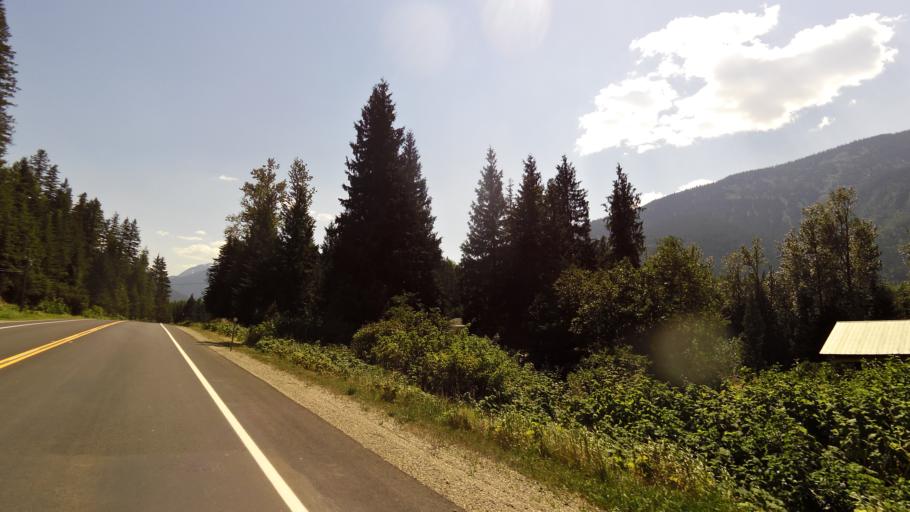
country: CA
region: British Columbia
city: Revelstoke
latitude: 50.9482
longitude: -118.4820
